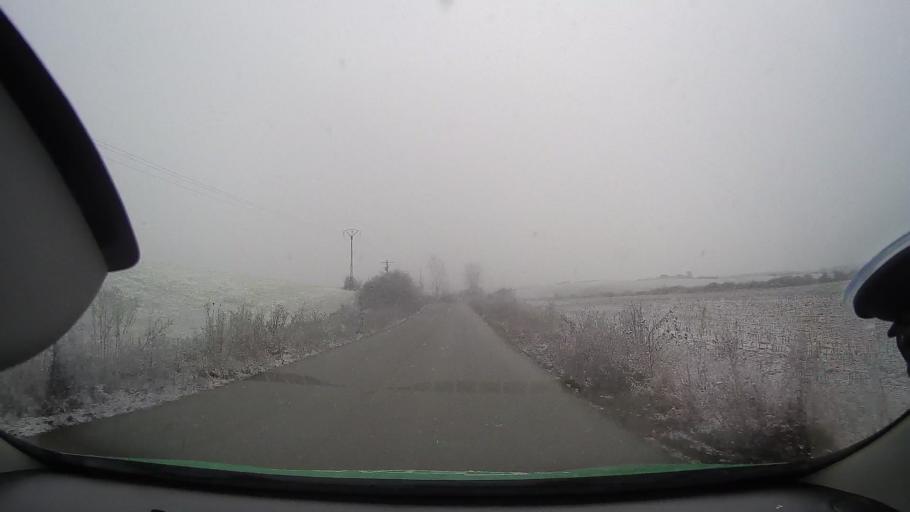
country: RO
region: Alba
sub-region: Comuna Noslac
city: Noslac
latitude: 46.3761
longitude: 23.9112
